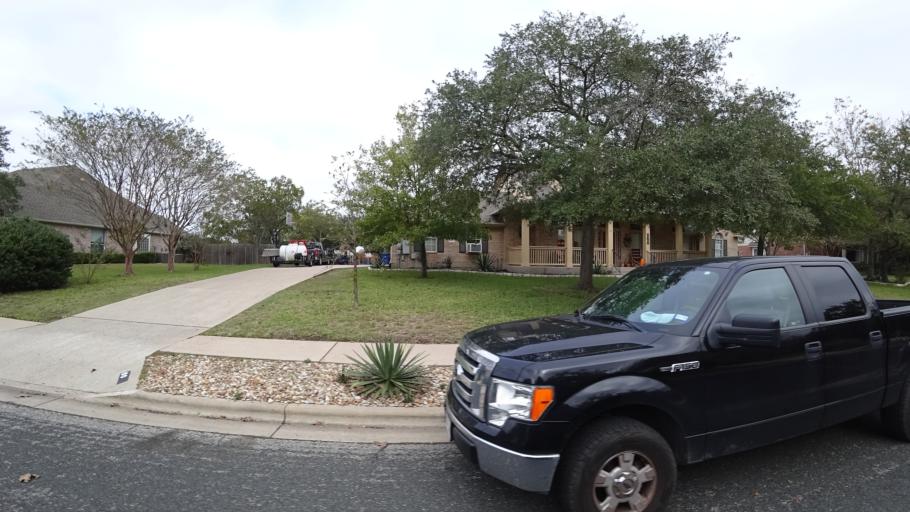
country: US
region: Texas
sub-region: Travis County
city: Shady Hollow
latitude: 30.2211
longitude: -97.8785
